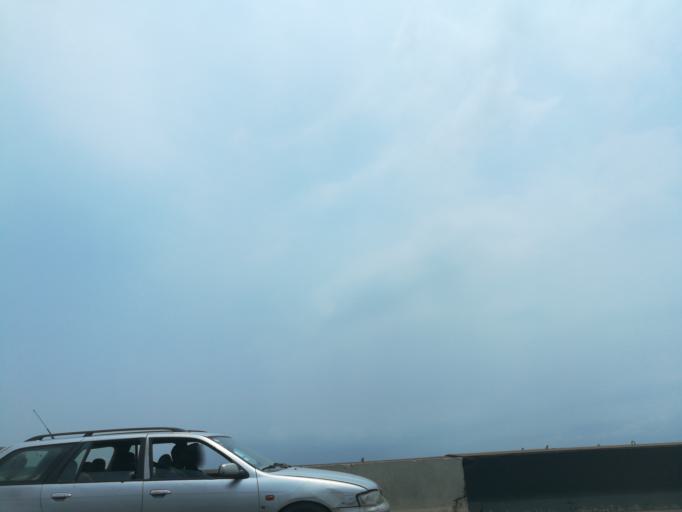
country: NG
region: Lagos
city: Somolu
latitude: 6.5303
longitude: 3.4021
